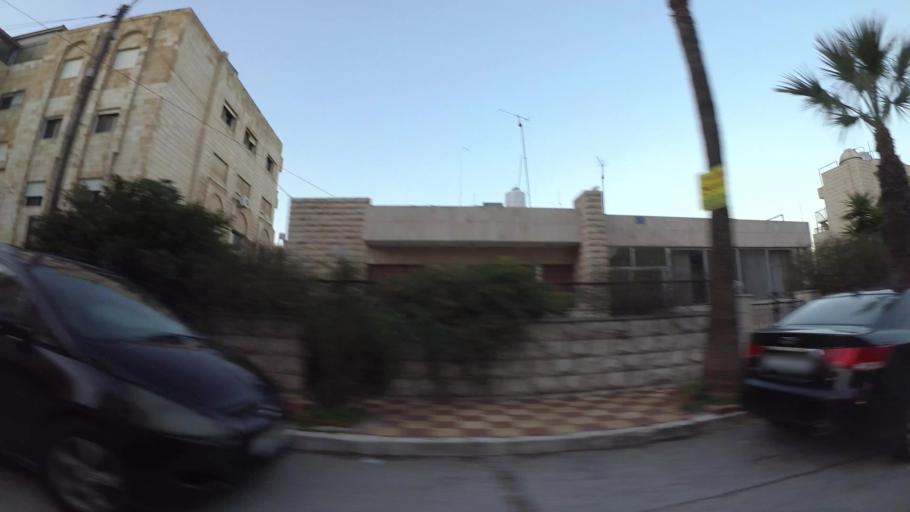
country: JO
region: Amman
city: Al Jubayhah
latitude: 31.9911
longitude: 35.8887
